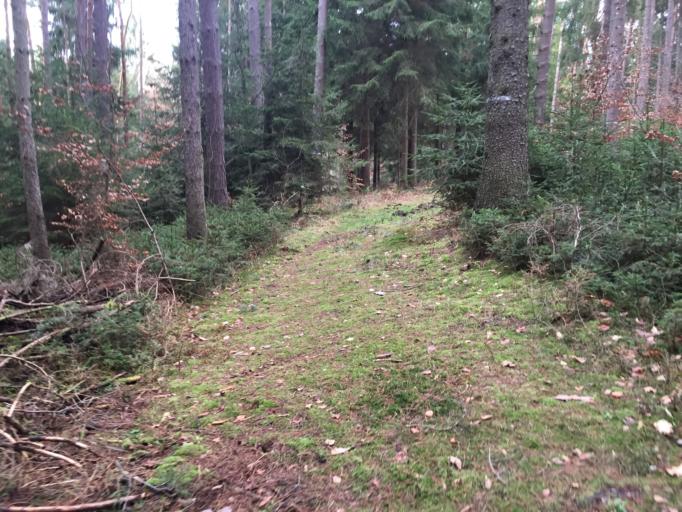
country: DE
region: Thuringia
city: Bobeck
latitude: 50.8896
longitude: 11.7849
